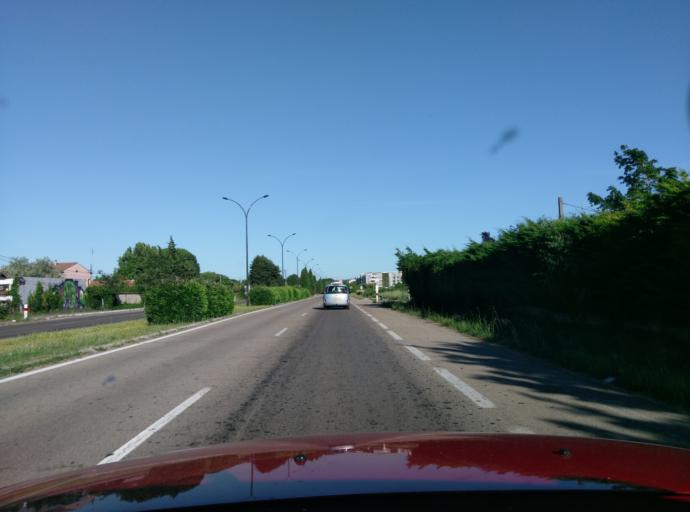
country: FR
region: Languedoc-Roussillon
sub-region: Departement du Gard
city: Rodilhan
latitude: 43.8359
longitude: 4.4006
